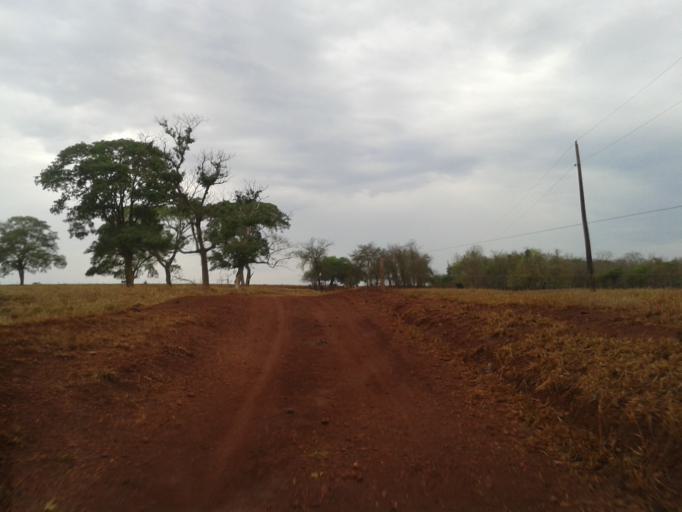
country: BR
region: Minas Gerais
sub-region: Santa Vitoria
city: Santa Vitoria
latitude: -18.8546
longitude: -49.8282
